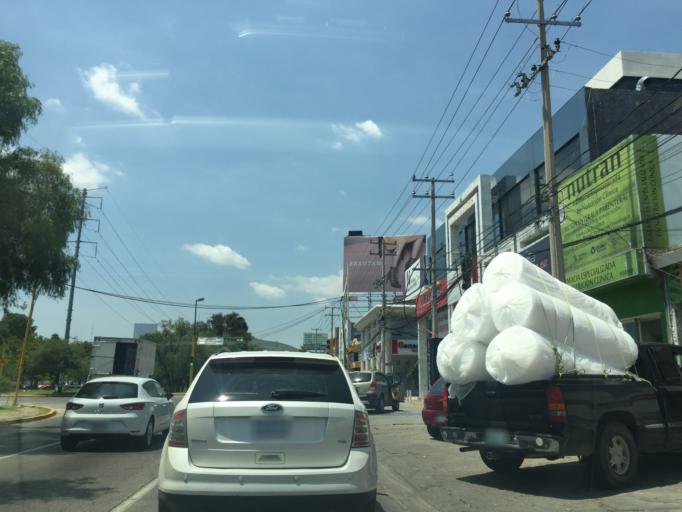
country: MX
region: Guanajuato
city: Leon
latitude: 21.1559
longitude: -101.6873
